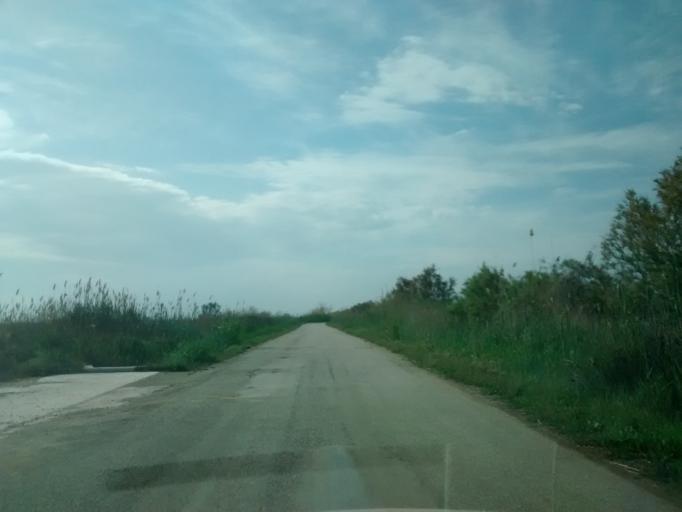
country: ES
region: Catalonia
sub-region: Provincia de Tarragona
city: Deltebre
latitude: 40.6887
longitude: 0.8472
